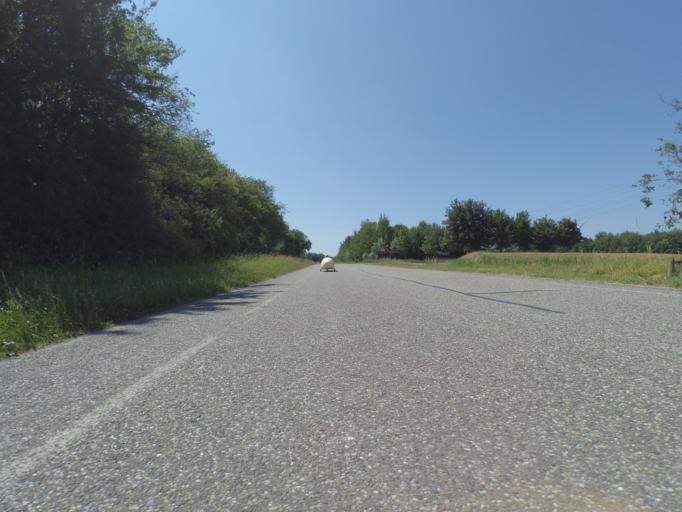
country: NL
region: North Brabant
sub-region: Gemeente Woensdrecht
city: Woensdrecht
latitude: 51.4300
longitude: 4.2388
